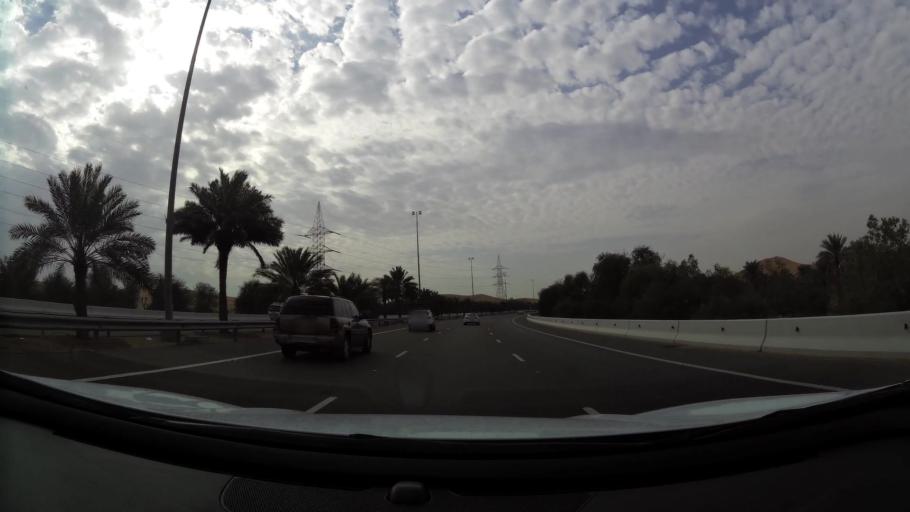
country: AE
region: Abu Dhabi
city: Al Ain
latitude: 24.2202
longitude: 55.5669
